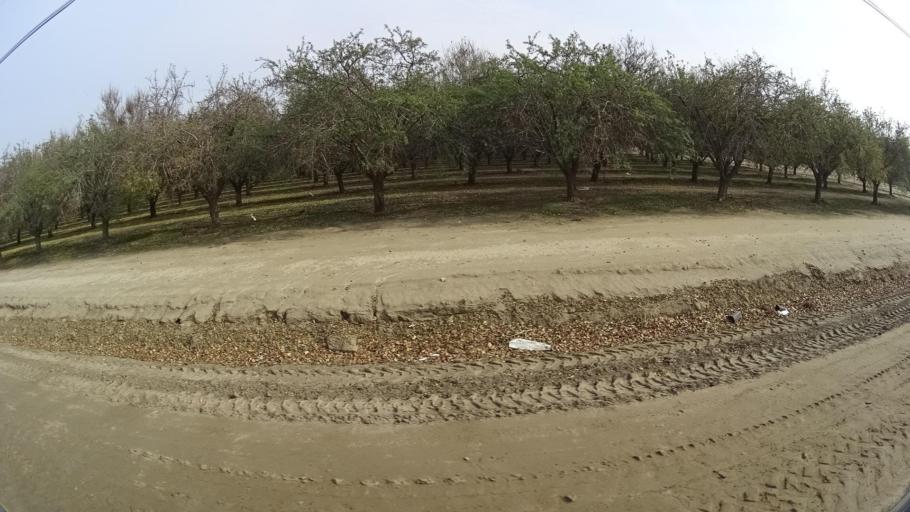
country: US
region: California
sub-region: Kern County
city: Arvin
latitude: 35.1585
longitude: -118.8509
